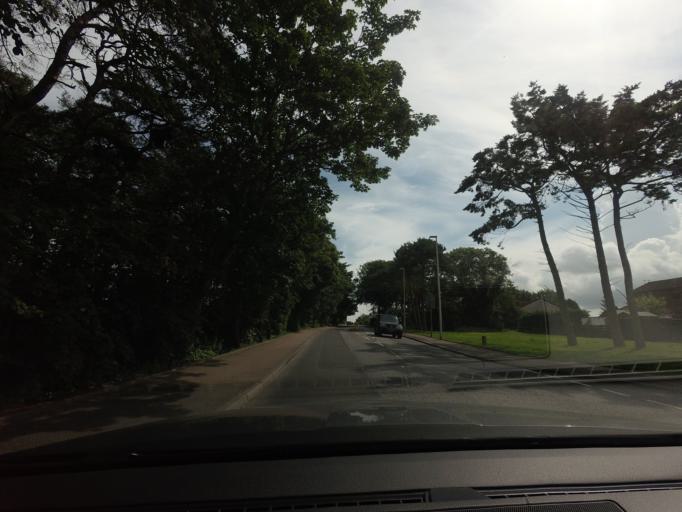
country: GB
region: Scotland
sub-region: Aberdeenshire
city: Mintlaw
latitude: 57.5253
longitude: -2.0086
